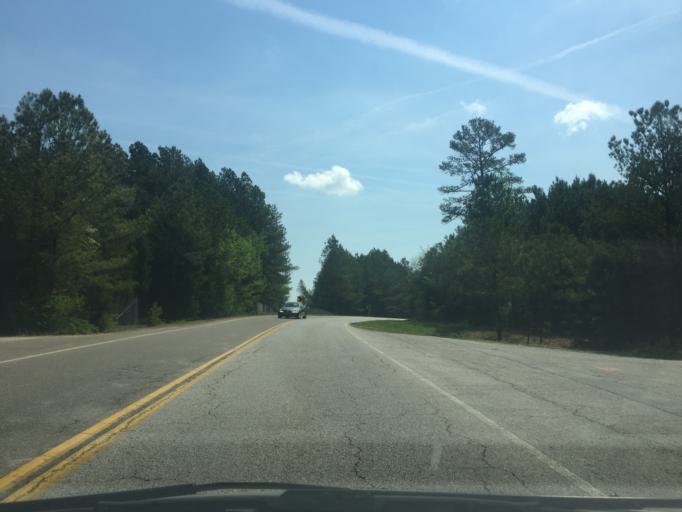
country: US
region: Tennessee
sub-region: Hamilton County
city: Harrison
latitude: 35.0829
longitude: -85.1542
